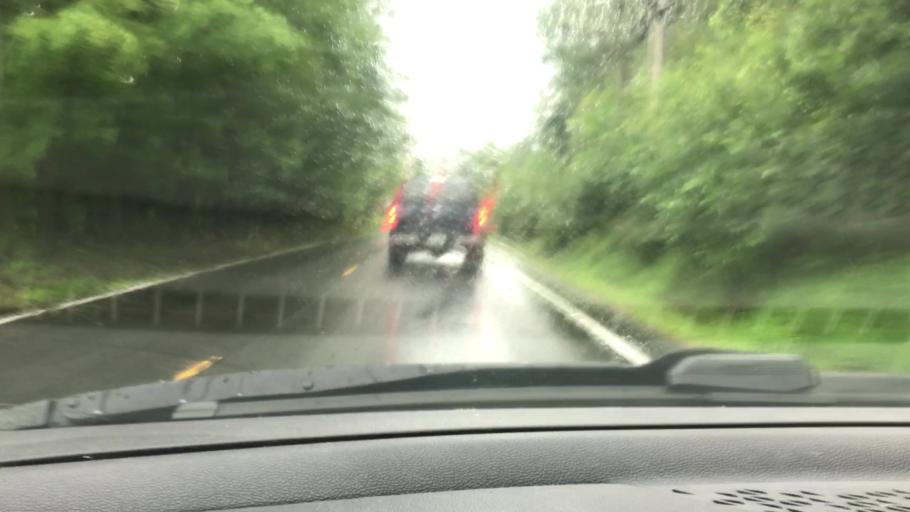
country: US
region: New Hampshire
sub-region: Rockingham County
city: Candia
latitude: 43.1604
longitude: -71.2420
